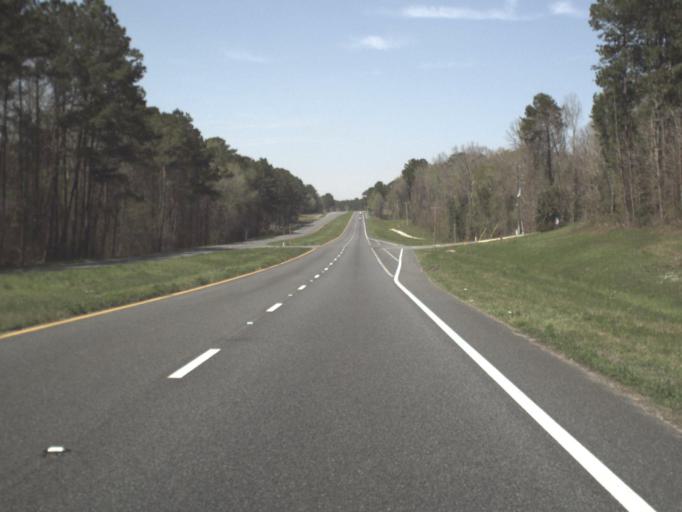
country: US
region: Florida
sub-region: Gadsden County
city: Midway
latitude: 30.5269
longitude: -84.4710
